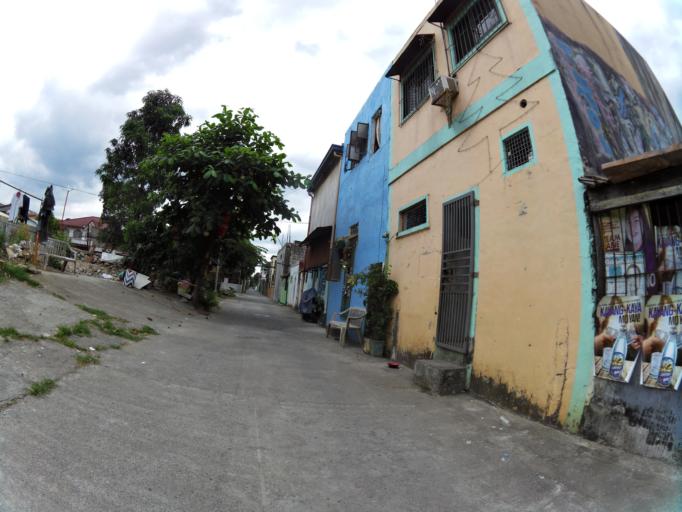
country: PH
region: Calabarzon
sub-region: Province of Rizal
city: Antipolo
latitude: 14.6402
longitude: 121.1118
